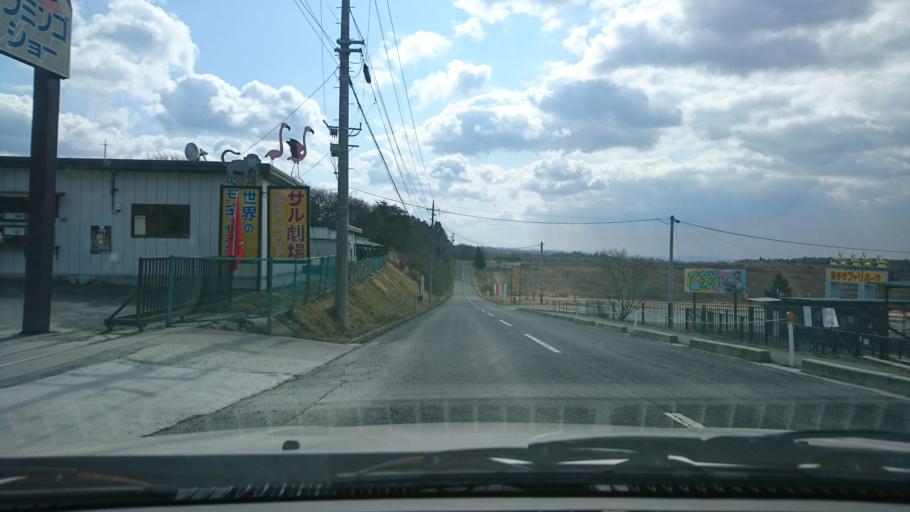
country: JP
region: Iwate
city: Ichinoseki
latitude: 38.8098
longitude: 141.2608
